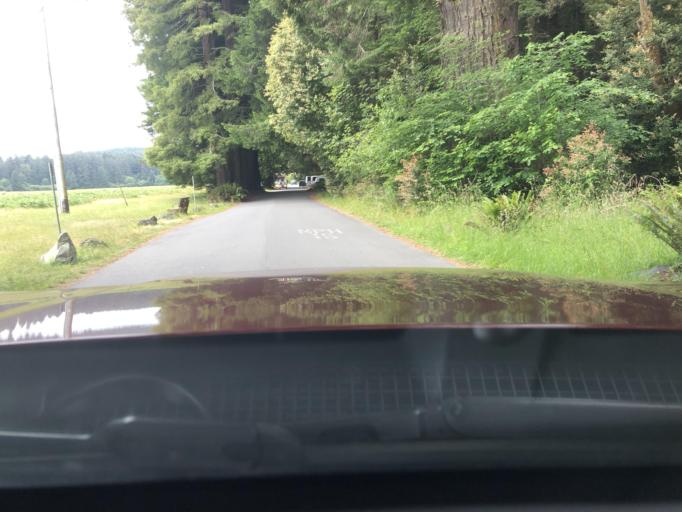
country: US
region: California
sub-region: Humboldt County
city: Westhaven-Moonstone
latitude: 41.3633
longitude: -124.0240
